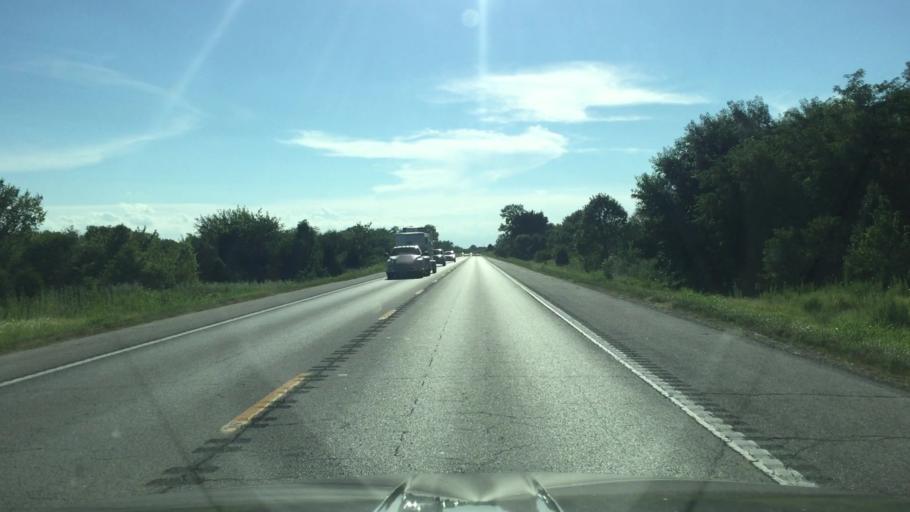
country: US
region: Missouri
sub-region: Pettis County
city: Sedalia
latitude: 38.6949
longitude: -93.1265
